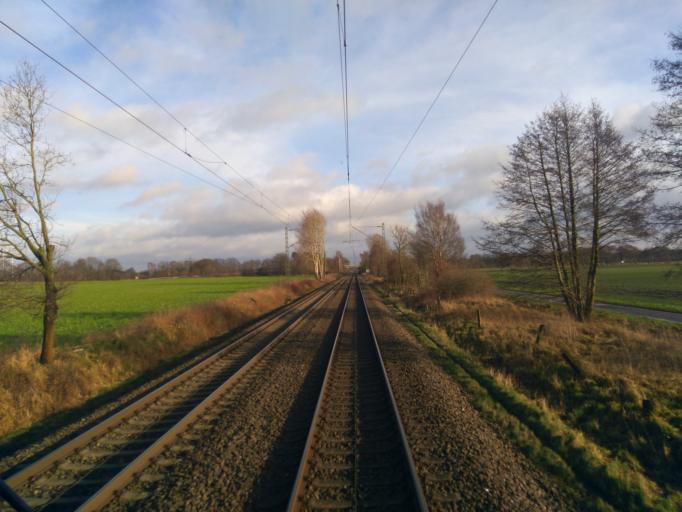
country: DE
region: Lower Saxony
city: Botersen
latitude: 53.1046
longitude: 9.3284
